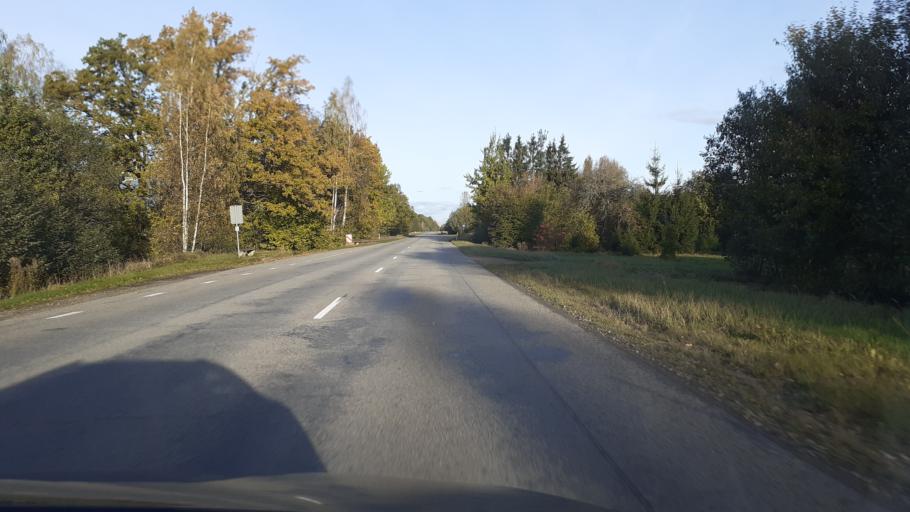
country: LV
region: Kuldigas Rajons
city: Kuldiga
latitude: 56.9406
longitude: 22.0248
